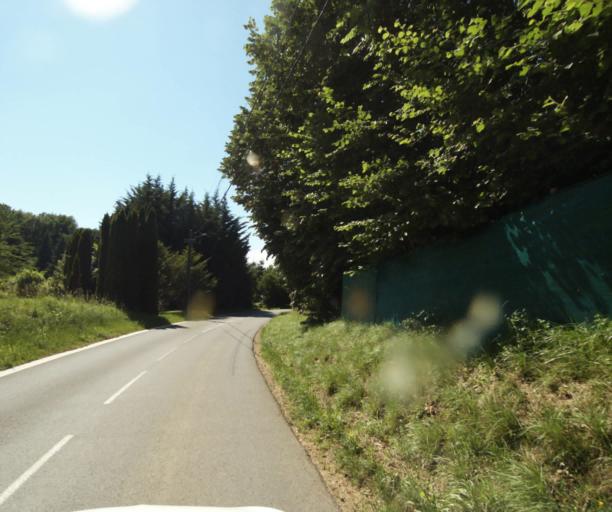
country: FR
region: Rhone-Alpes
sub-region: Departement de la Haute-Savoie
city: Bons-en-Chablais
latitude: 46.2552
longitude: 6.3817
